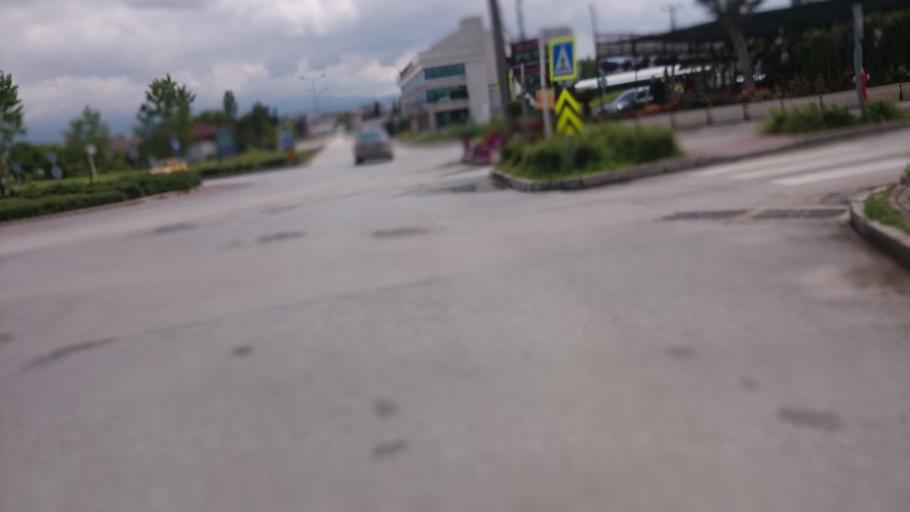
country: TR
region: Bursa
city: Niluefer
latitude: 40.2349
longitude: 28.9105
